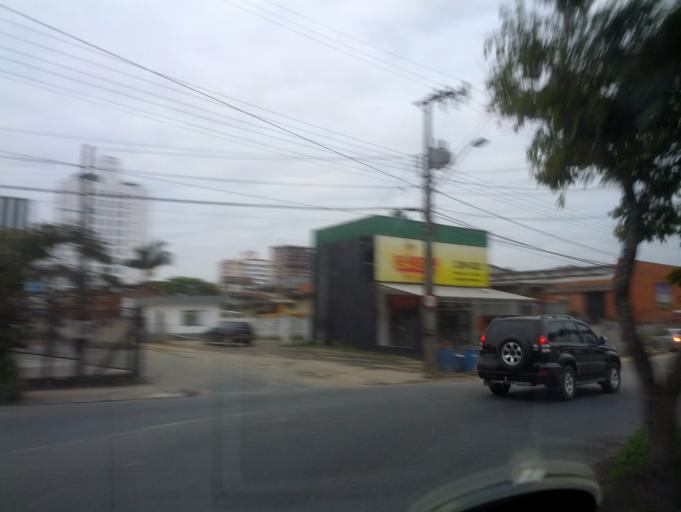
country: BR
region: Santa Catarina
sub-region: Blumenau
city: Blumenau
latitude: -26.8834
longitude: -49.0837
